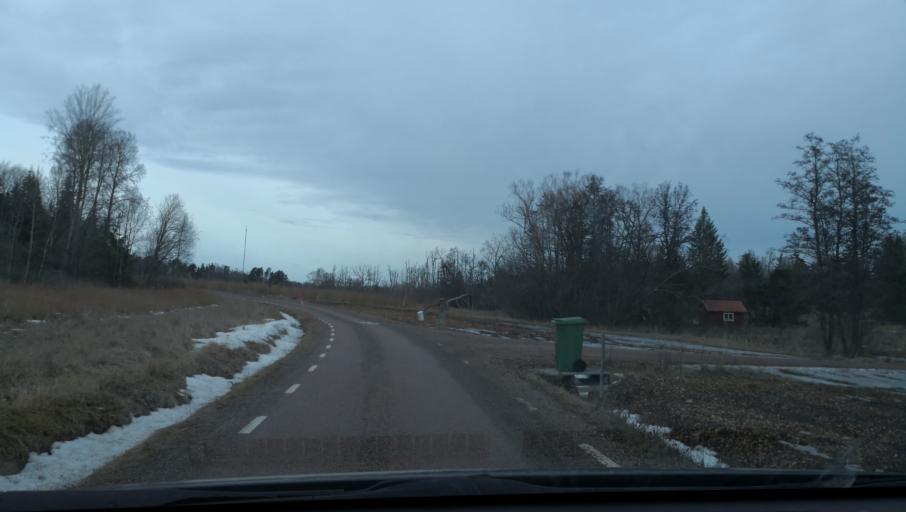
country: SE
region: Vaestmanland
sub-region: Vasteras
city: Skultuna
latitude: 59.6102
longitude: 16.4113
